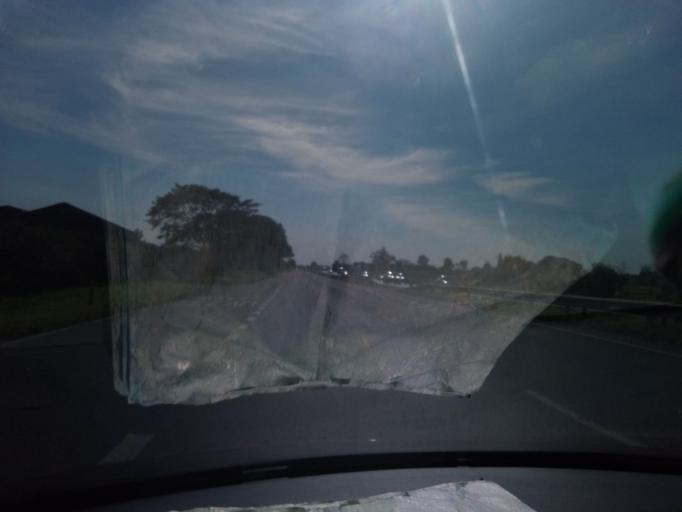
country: GB
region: England
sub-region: Stockton-on-Tees
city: Yarm
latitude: 54.4090
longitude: -1.3186
